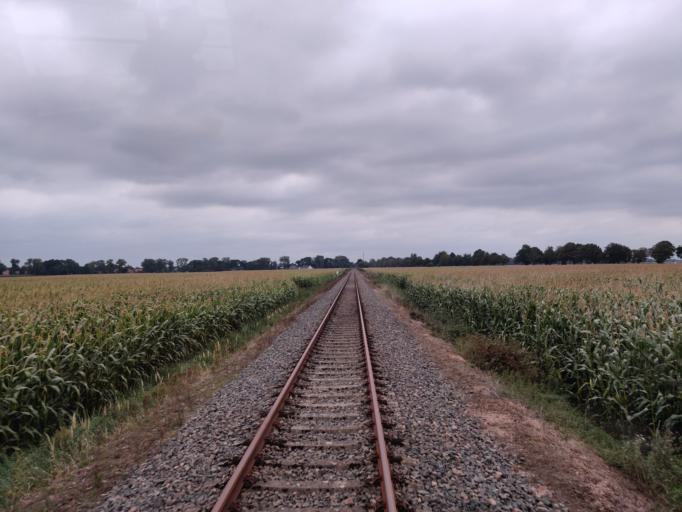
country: DE
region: Lower Saxony
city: Vollersode
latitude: 53.3036
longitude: 8.9713
